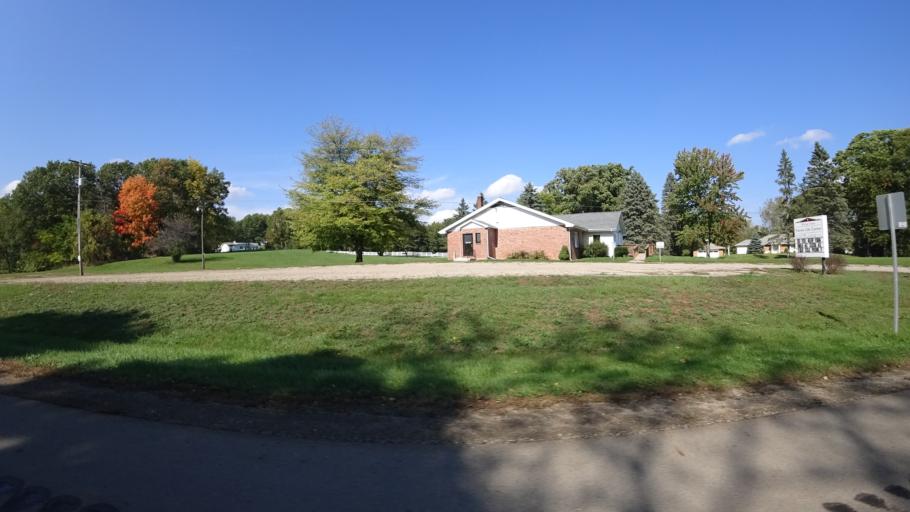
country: US
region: Michigan
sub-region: Jackson County
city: Concord
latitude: 42.1929
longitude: -84.6076
